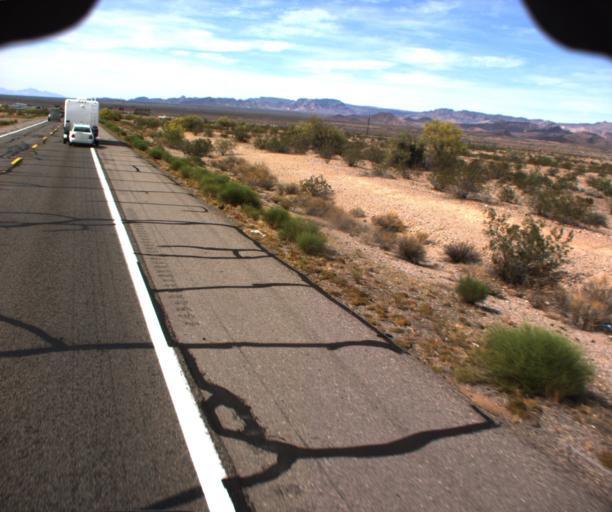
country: US
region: Arizona
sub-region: Mohave County
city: Desert Hills
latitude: 34.7149
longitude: -114.3087
